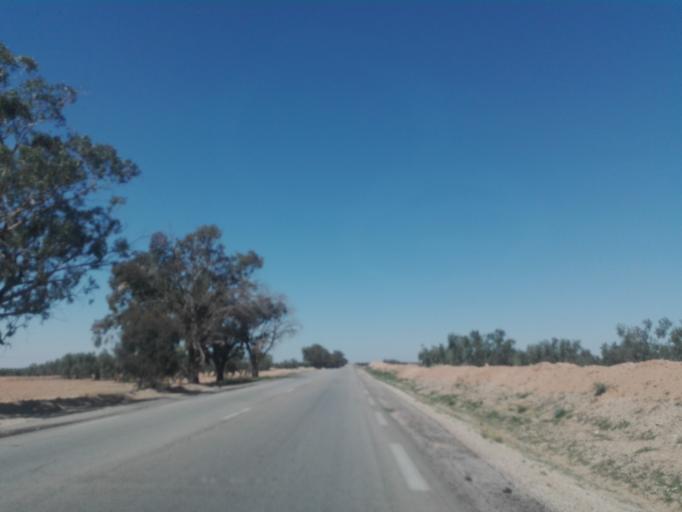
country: TN
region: Safaqis
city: Bi'r `Ali Bin Khalifah
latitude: 34.7572
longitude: 10.3214
